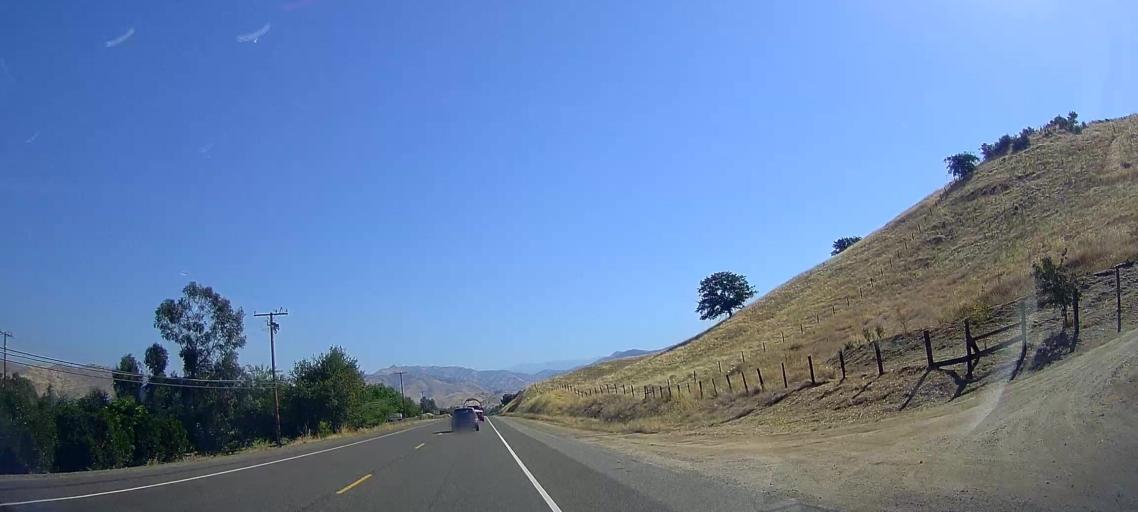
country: US
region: California
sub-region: Tulare County
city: Woodlake
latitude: 36.3664
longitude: -119.0340
